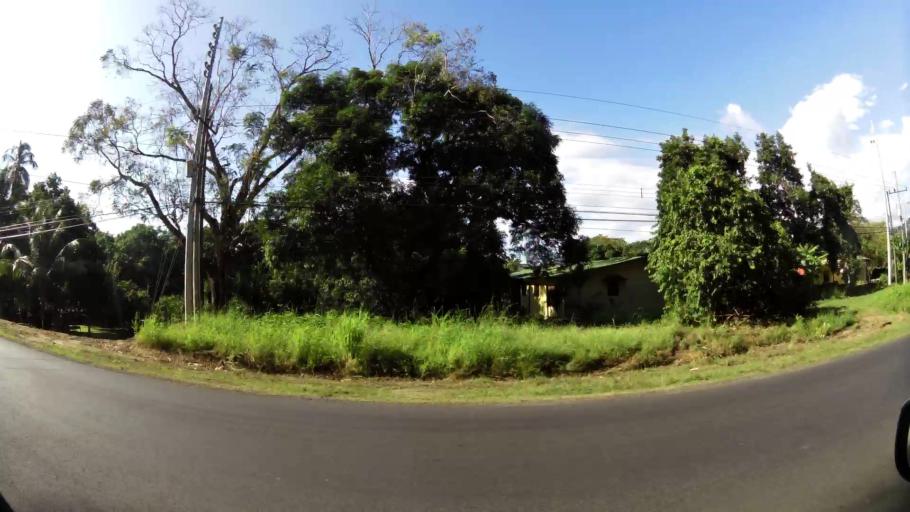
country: CR
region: Puntarenas
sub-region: Canton de Garabito
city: Jaco
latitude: 9.5982
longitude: -84.6176
